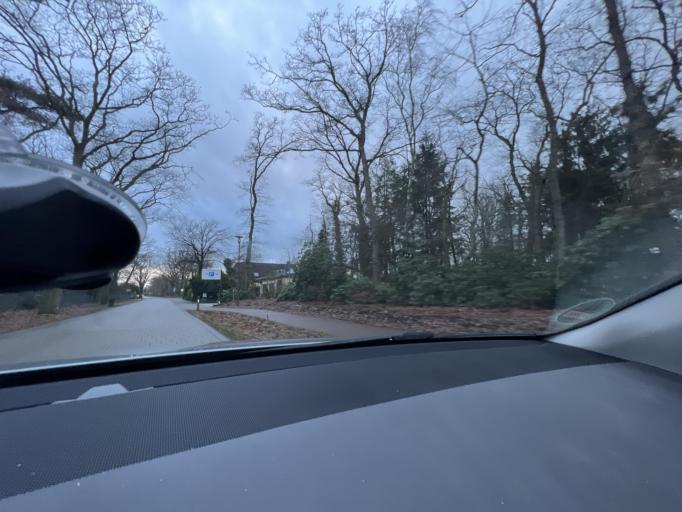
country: DE
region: Lower Saxony
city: Hatten
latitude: 53.0494
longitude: 8.2983
